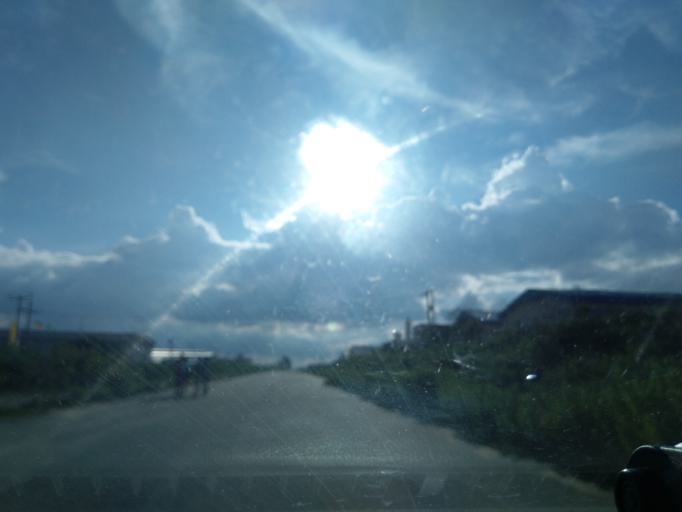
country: NG
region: Abuja Federal Capital Territory
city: Abuja
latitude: 9.0297
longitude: 7.4038
